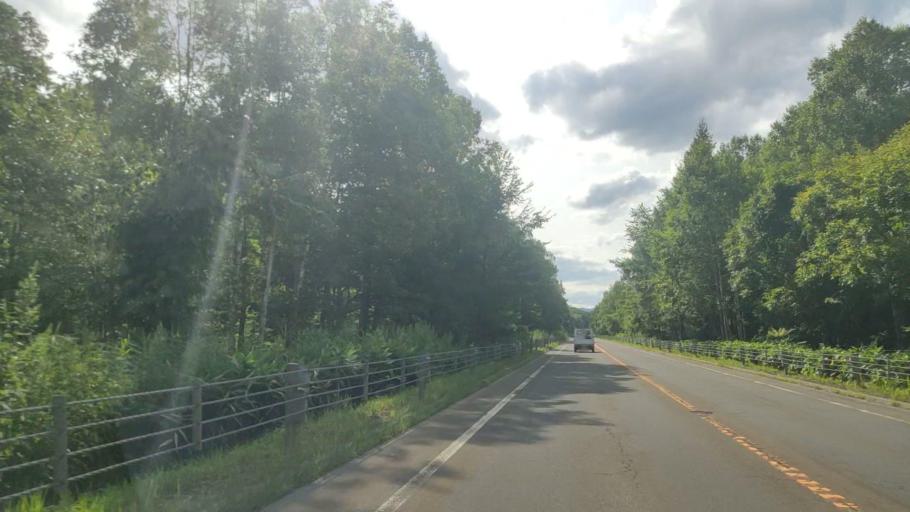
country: JP
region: Hokkaido
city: Nayoro
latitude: 44.3853
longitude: 142.4080
